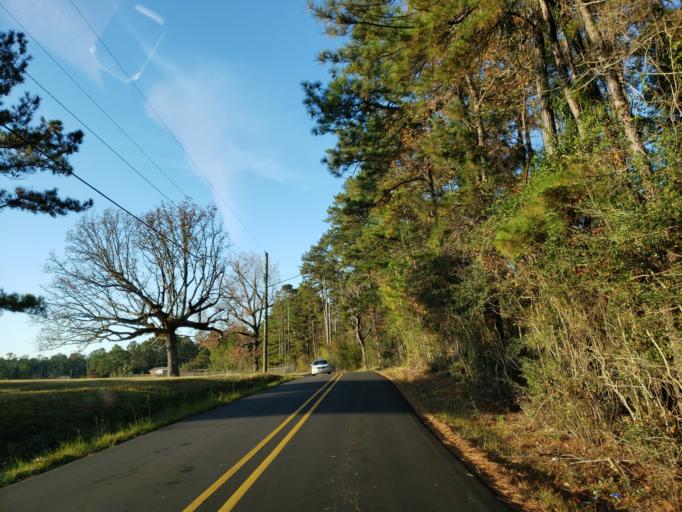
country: US
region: Mississippi
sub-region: Lamar County
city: Arnold Line
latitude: 31.3516
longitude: -89.3583
